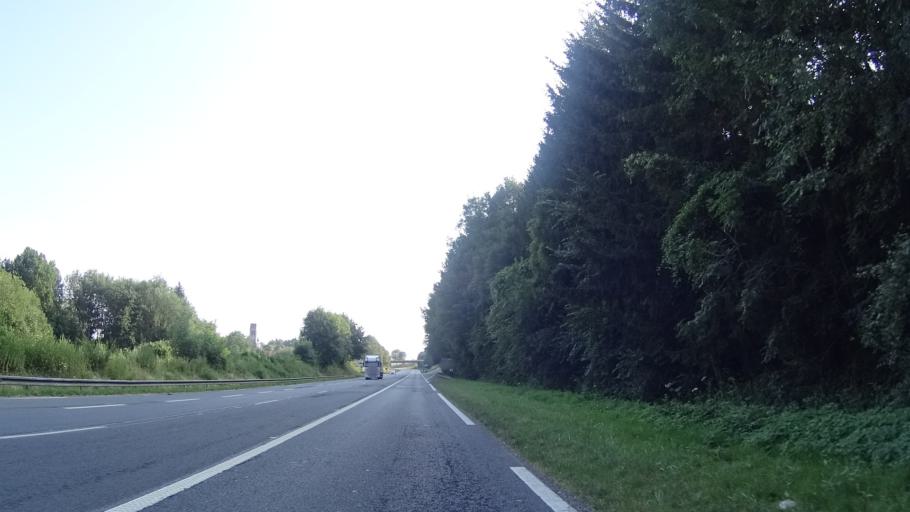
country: FR
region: Ile-de-France
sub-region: Departement du Val-d'Oise
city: Luzarches
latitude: 49.1077
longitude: 2.4273
